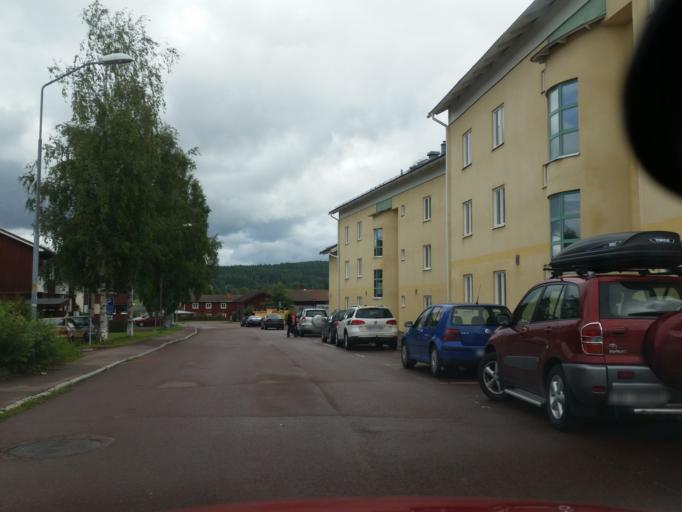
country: SE
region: Dalarna
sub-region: Leksand Municipality
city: Leksand
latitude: 60.7301
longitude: 15.0019
